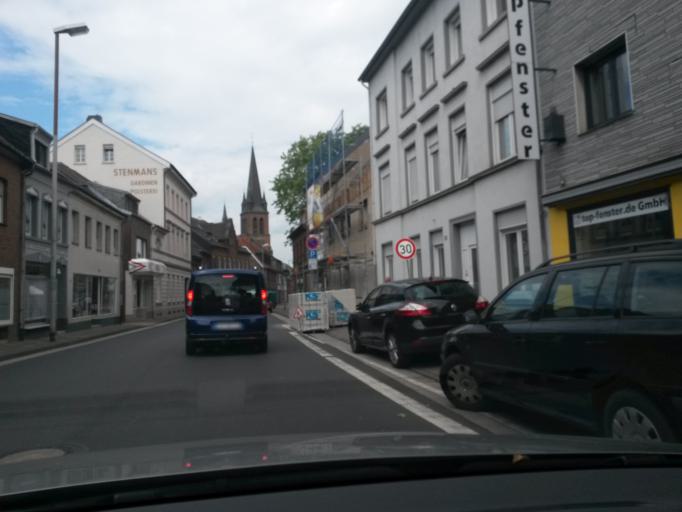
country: DE
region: North Rhine-Westphalia
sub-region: Regierungsbezirk Dusseldorf
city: Grefrath
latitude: 51.3244
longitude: 6.3800
